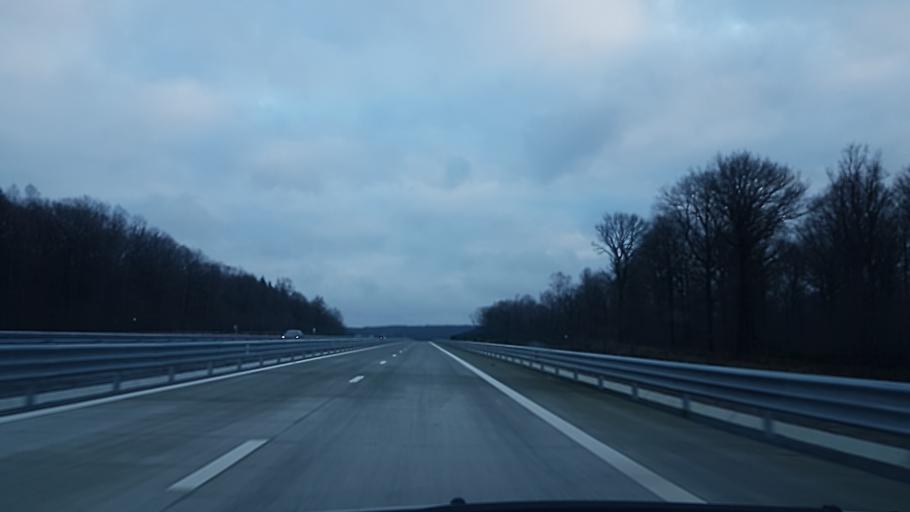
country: BE
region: Wallonia
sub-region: Province de Namur
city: Couvin
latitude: 50.0194
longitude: 4.5274
